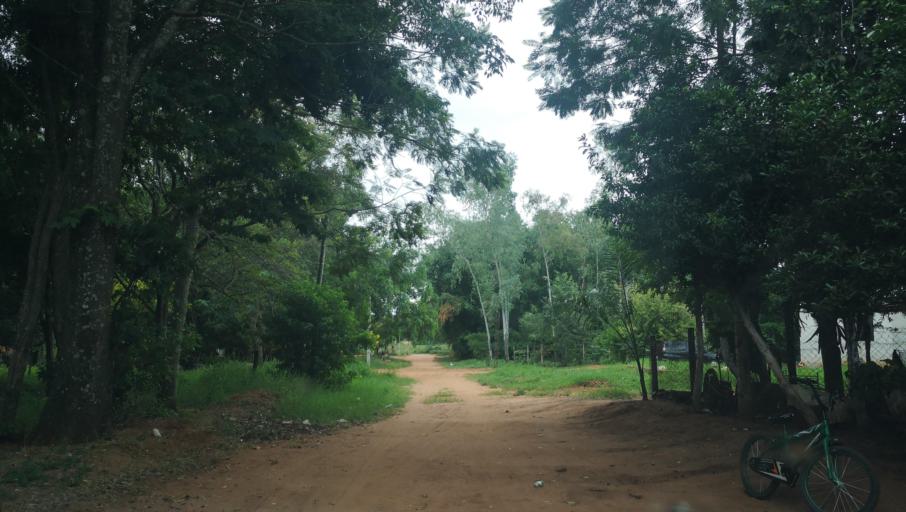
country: PY
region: San Pedro
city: Capiibary
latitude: -24.7378
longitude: -56.0195
